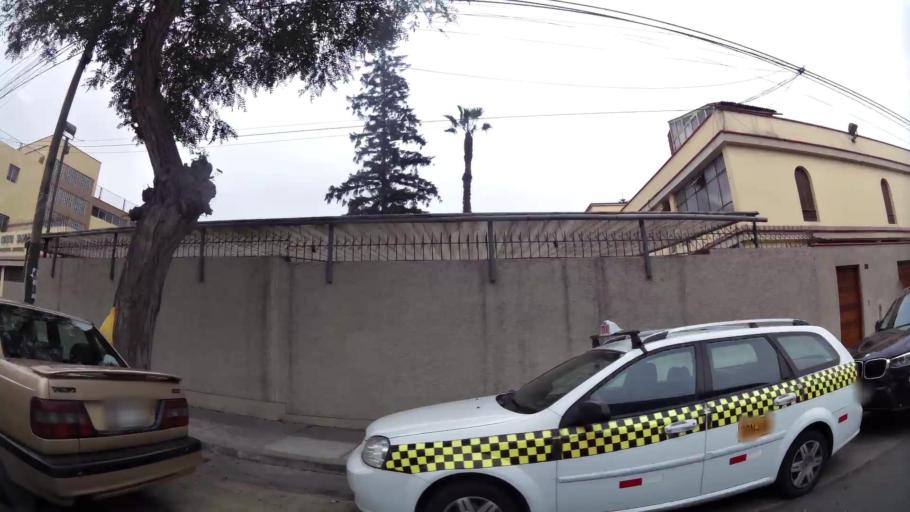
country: PE
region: Lima
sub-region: Lima
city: Surco
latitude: -12.1271
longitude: -76.9959
